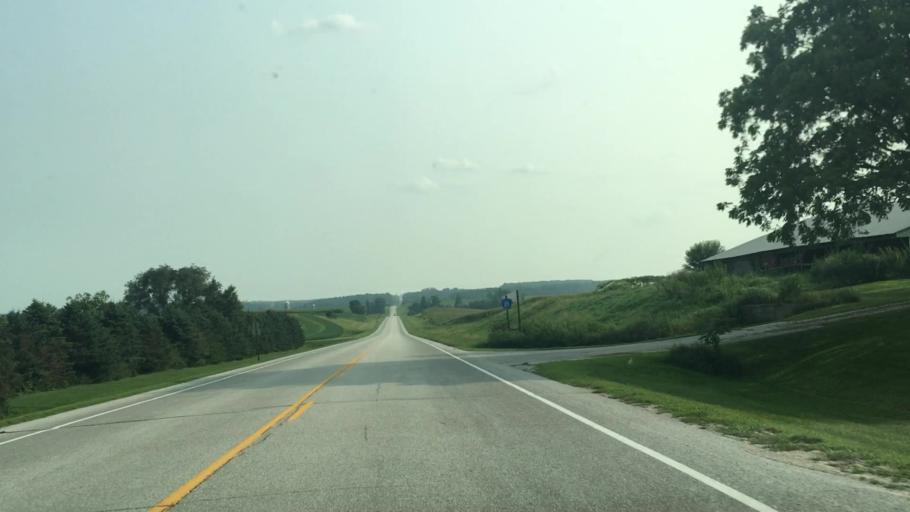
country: US
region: Minnesota
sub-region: Fillmore County
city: Harmony
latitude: 43.6158
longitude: -91.9299
